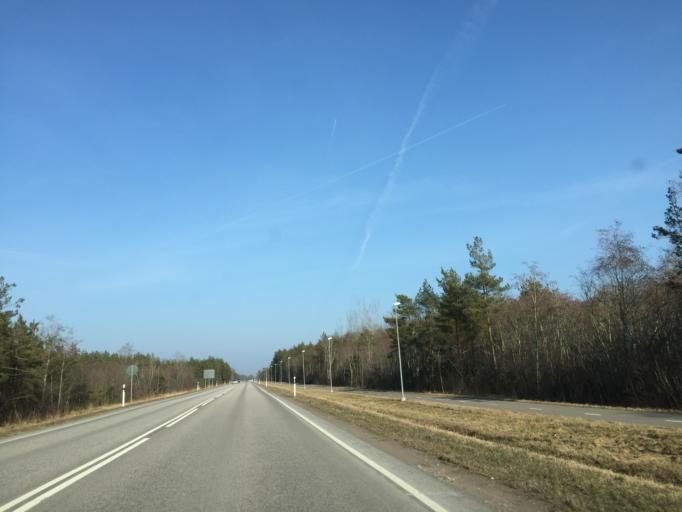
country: EE
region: Saare
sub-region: Kuressaare linn
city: Kuressaare
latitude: 58.2327
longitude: 22.4183
